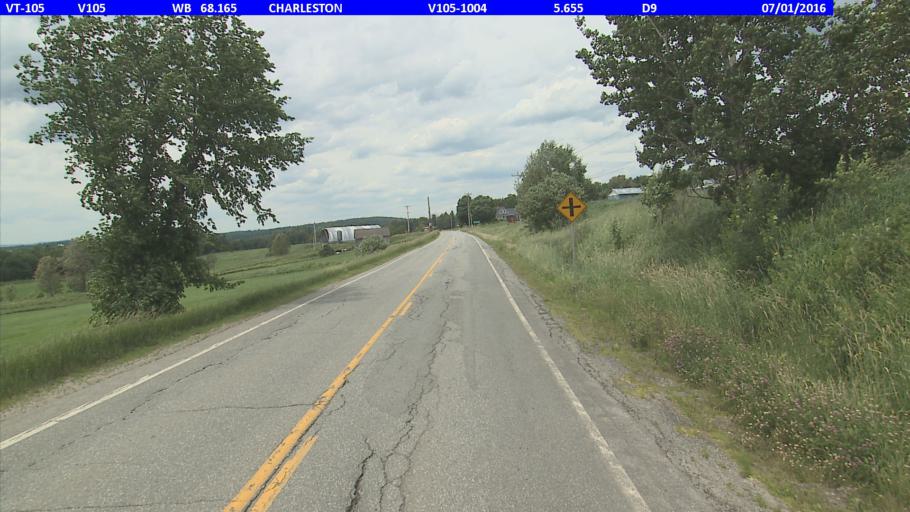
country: US
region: Vermont
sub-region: Orleans County
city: Newport
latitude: 44.8452
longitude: -72.0162
